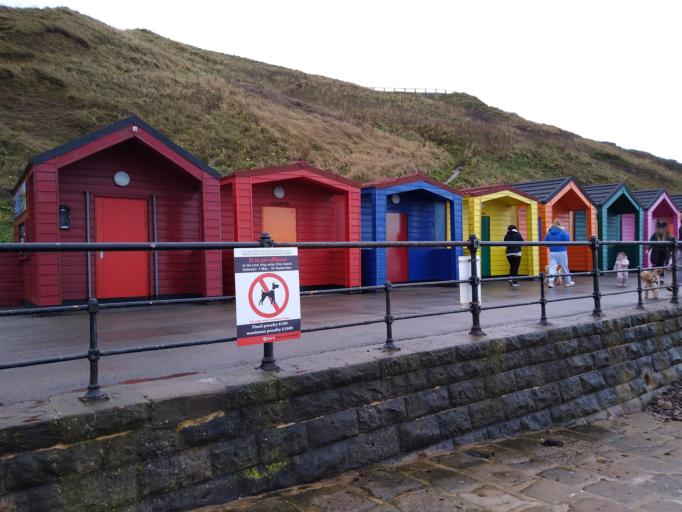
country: GB
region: England
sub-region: Redcar and Cleveland
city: Saltburn-by-the-Sea
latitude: 54.5868
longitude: -0.9729
